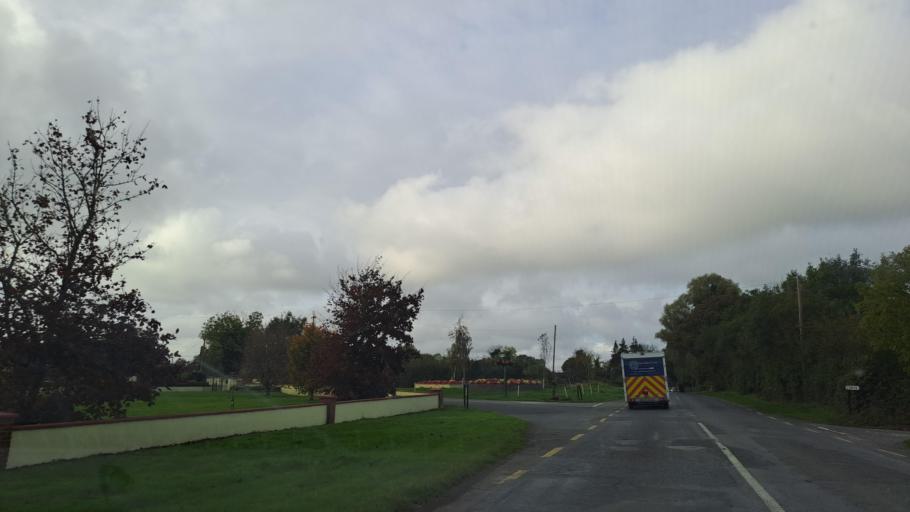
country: IE
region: Leinster
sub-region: An Mhi
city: Navan
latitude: 53.7422
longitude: -6.7156
